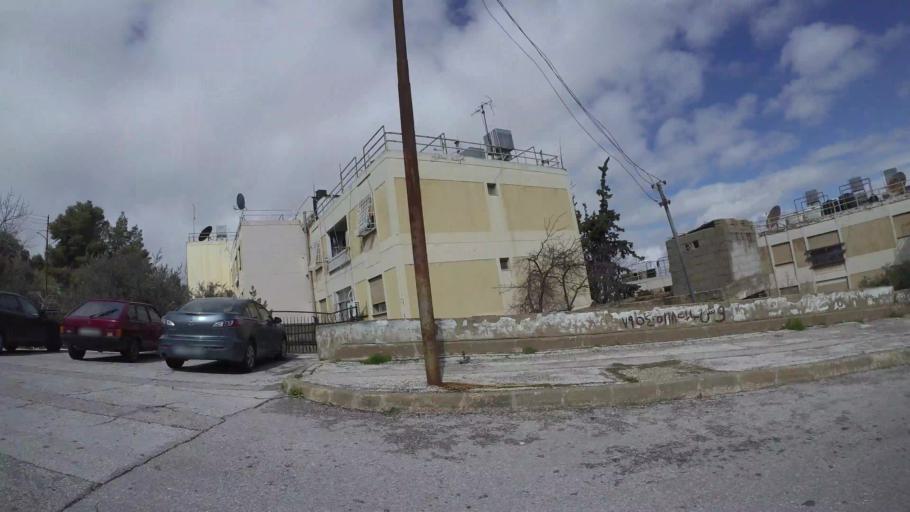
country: JO
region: Amman
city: Al Jubayhah
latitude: 32.0571
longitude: 35.8812
